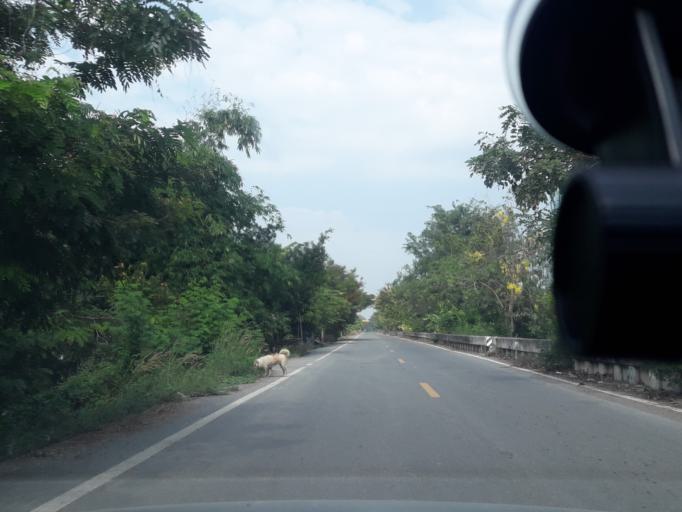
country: TH
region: Sara Buri
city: Nong Khae
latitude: 14.2410
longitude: 100.8913
